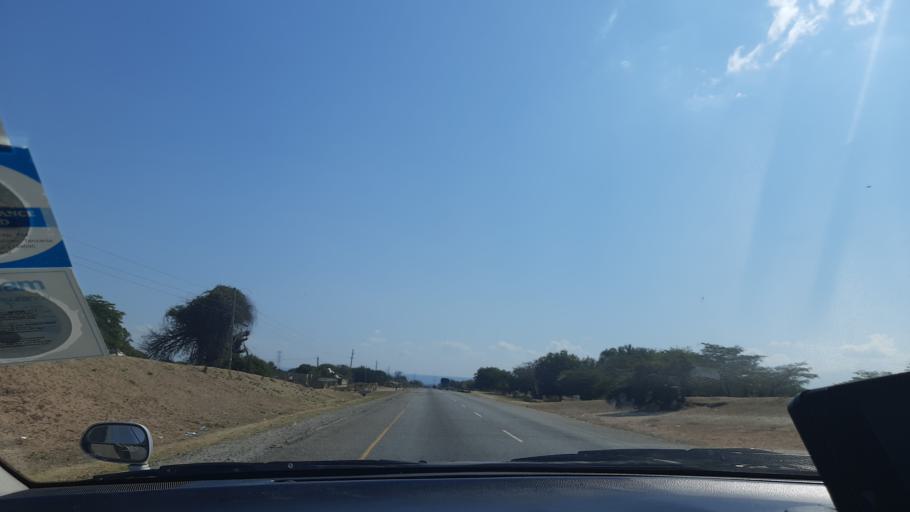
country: TZ
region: Singida
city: Kintinku
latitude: -5.8797
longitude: 35.1279
